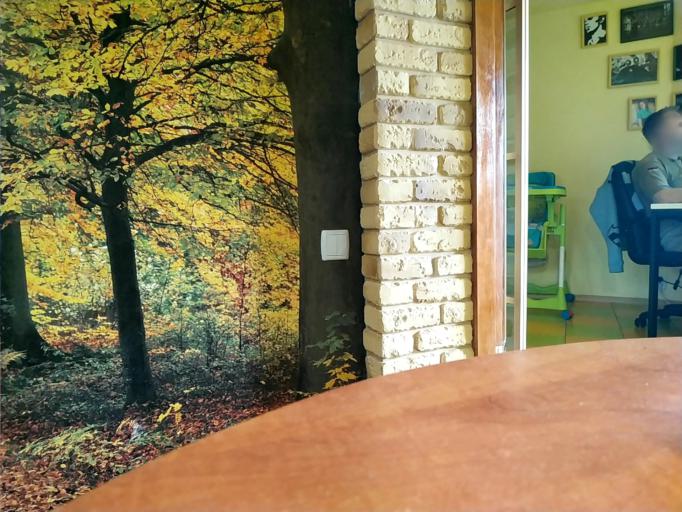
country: RU
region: Tverskaya
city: Vasil'yevskiy Mokh
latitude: 57.1995
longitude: 35.7479
